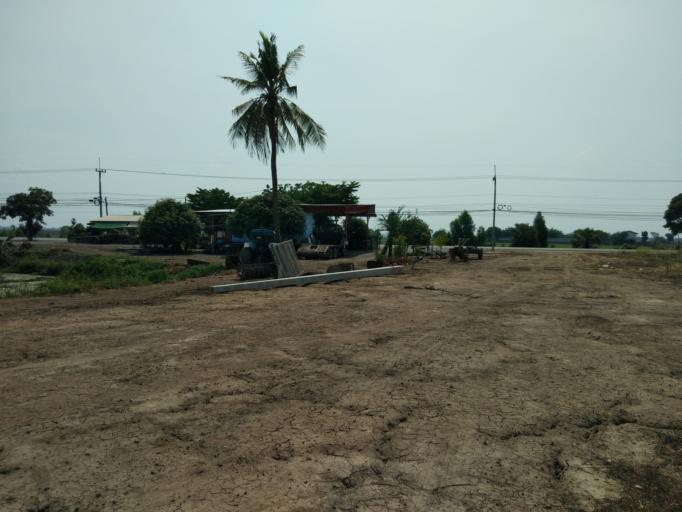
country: TH
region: Suphan Buri
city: Bang Pla Ma
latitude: 14.2861
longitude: 100.1326
